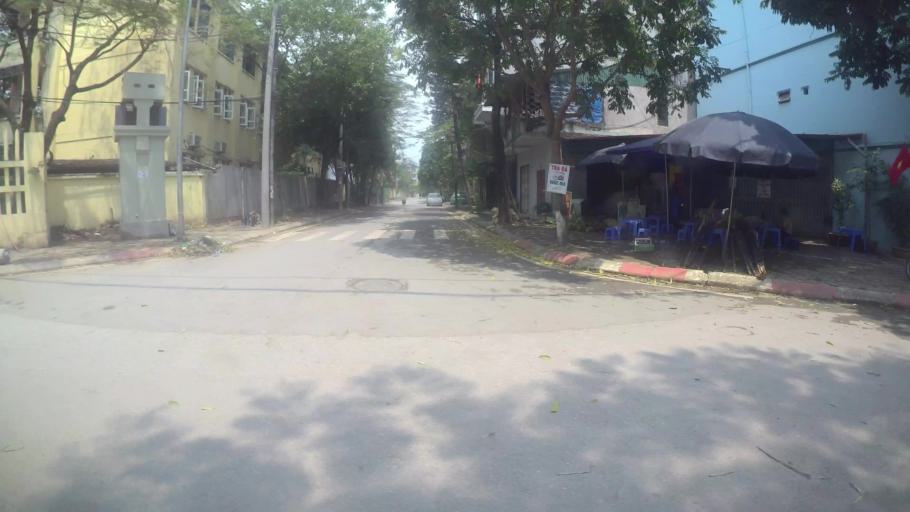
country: VN
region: Ha Noi
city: Tay Ho
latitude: 21.0859
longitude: 105.8099
